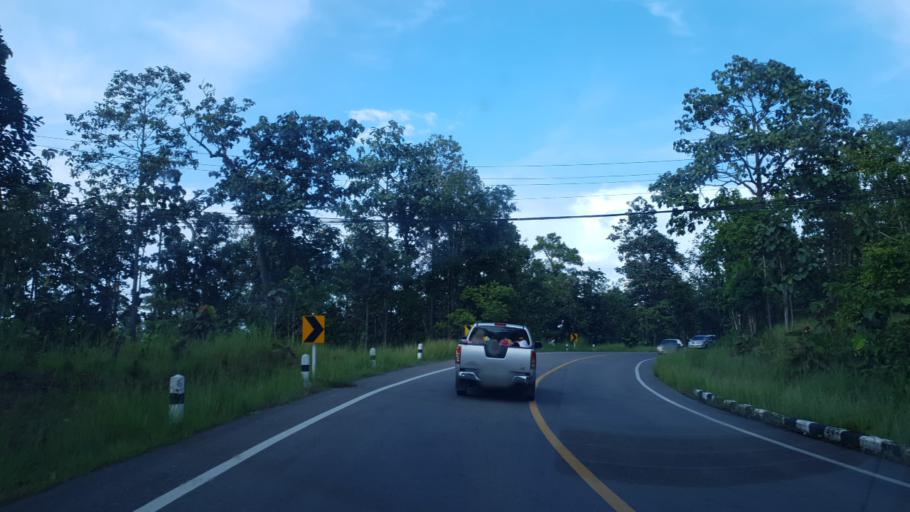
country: TH
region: Mae Hong Son
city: Khun Yuam
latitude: 18.7557
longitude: 97.9276
